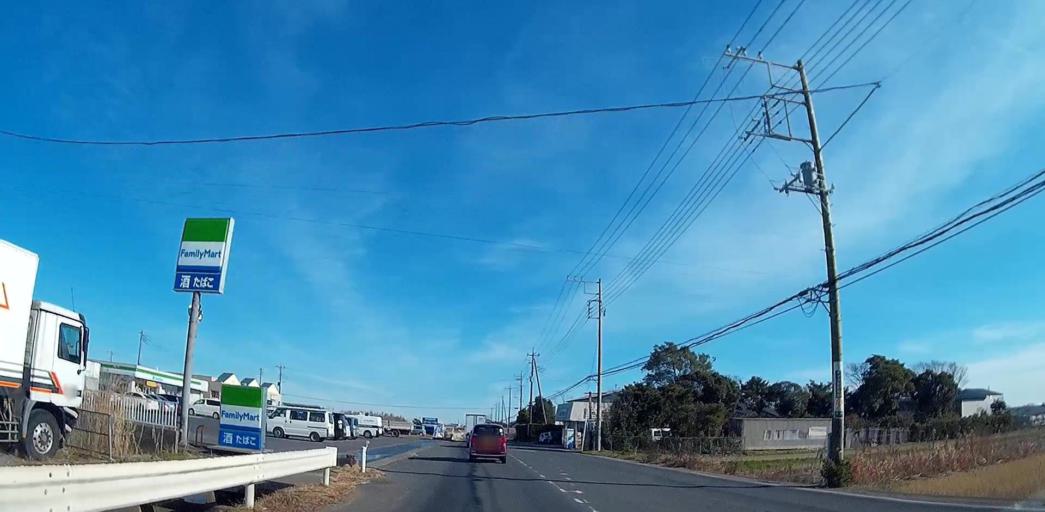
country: JP
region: Chiba
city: Asahi
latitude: 35.7435
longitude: 140.6164
